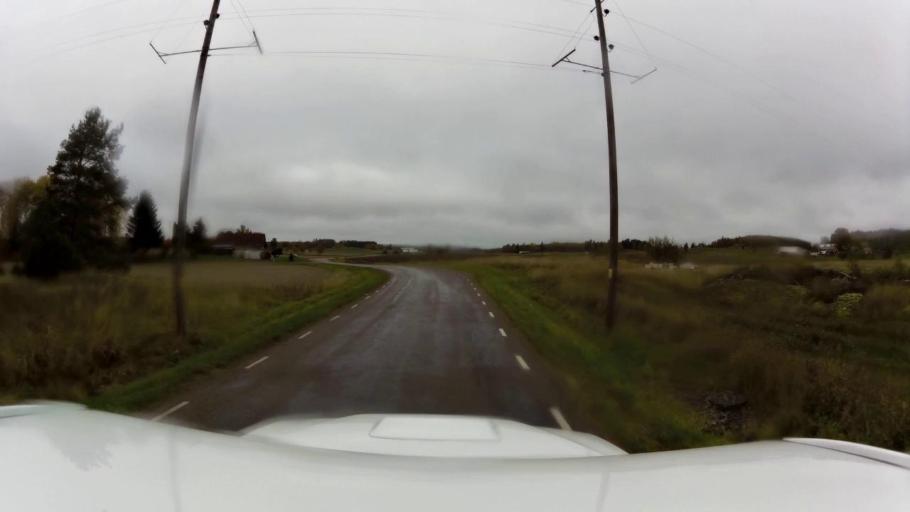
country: SE
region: OEstergoetland
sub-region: Linkopings Kommun
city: Linghem
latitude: 58.4669
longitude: 15.8250
